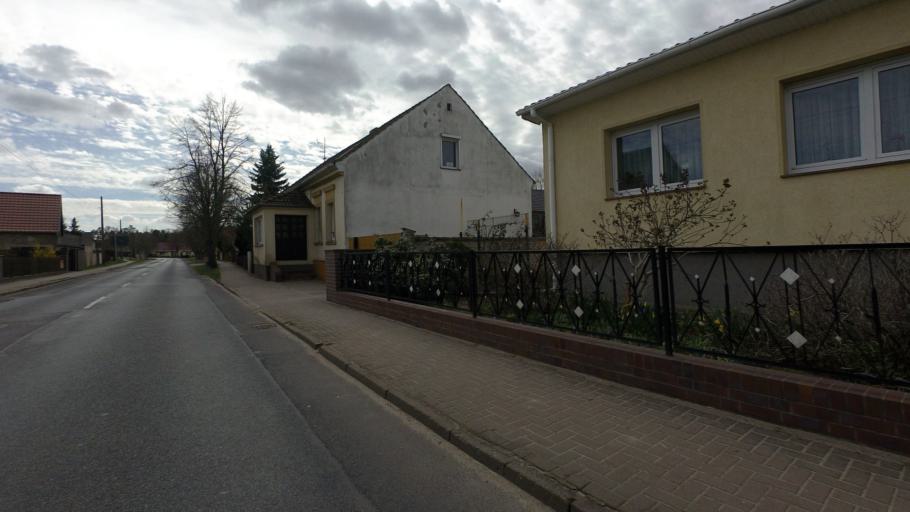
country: DE
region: Brandenburg
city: Wandlitz
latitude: 52.7541
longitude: 13.3724
